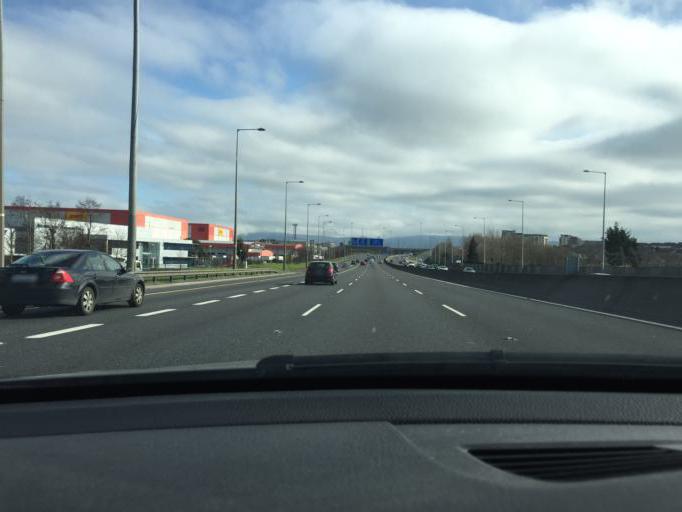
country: IE
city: Cherry Orchard
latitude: 53.3260
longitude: -6.3750
